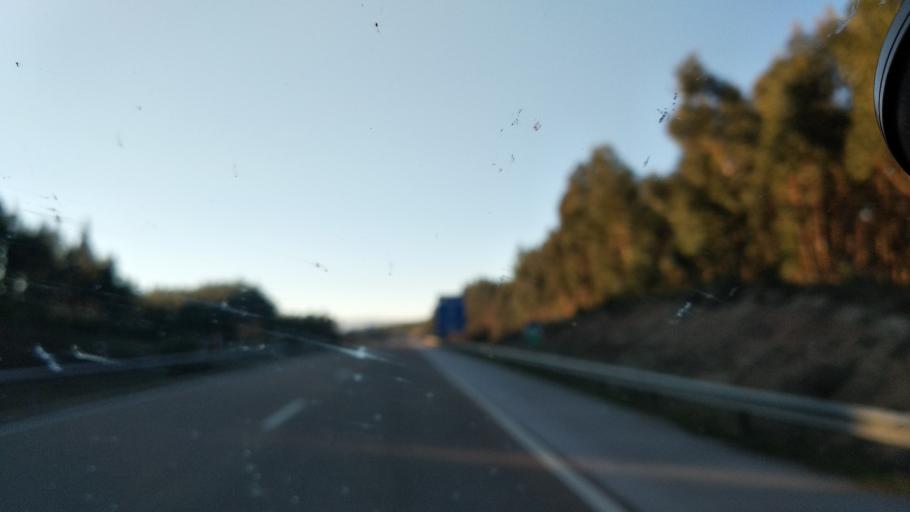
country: PT
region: Santarem
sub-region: Chamusca
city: Vila Nova da Barquinha
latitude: 39.4873
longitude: -8.4201
